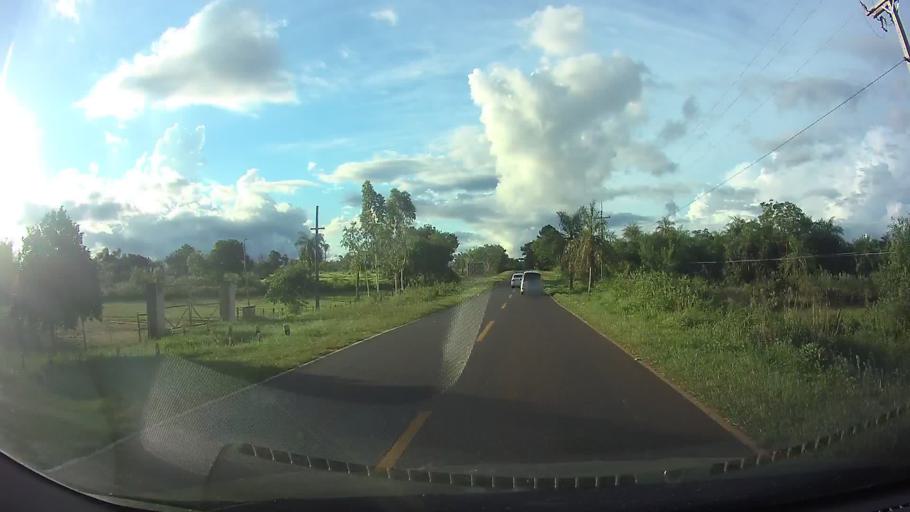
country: PY
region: Paraguari
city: Ybycui
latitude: -25.9936
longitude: -57.0532
